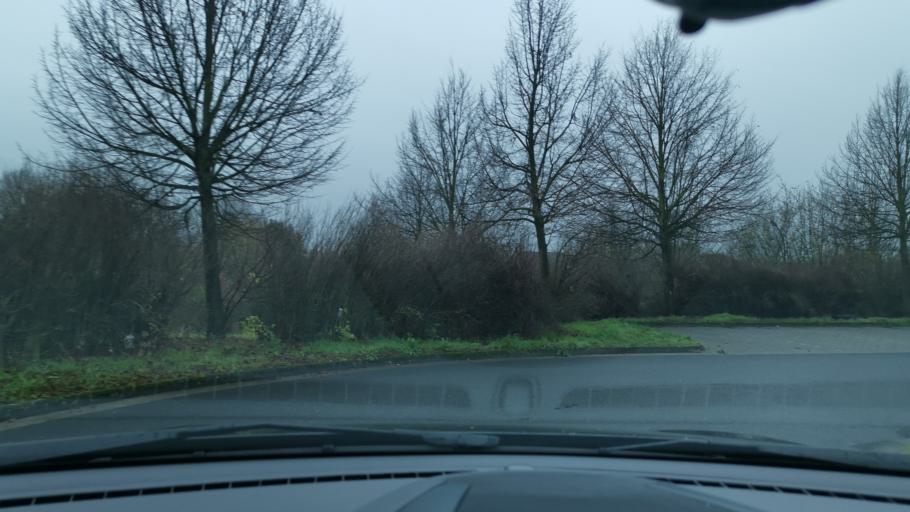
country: DE
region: North Rhine-Westphalia
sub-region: Regierungsbezirk Dusseldorf
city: Juchen
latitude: 51.1043
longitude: 6.5169
